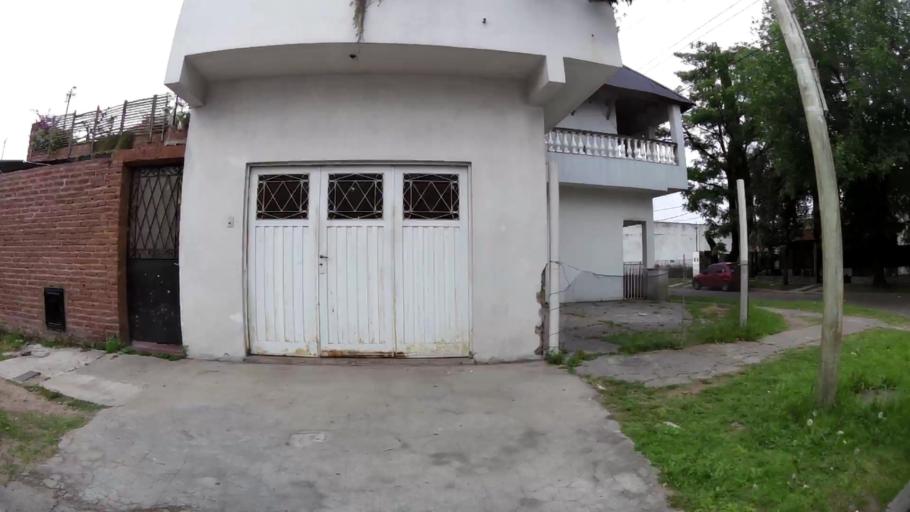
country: AR
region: Buenos Aires
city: San Justo
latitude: -34.7155
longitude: -58.5233
